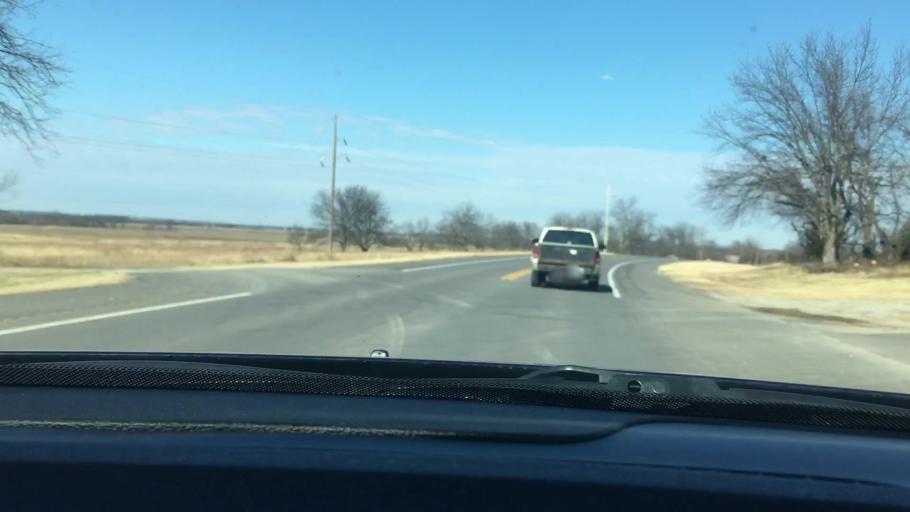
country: US
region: Oklahoma
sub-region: Garvin County
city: Wynnewood
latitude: 34.5790
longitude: -97.1419
